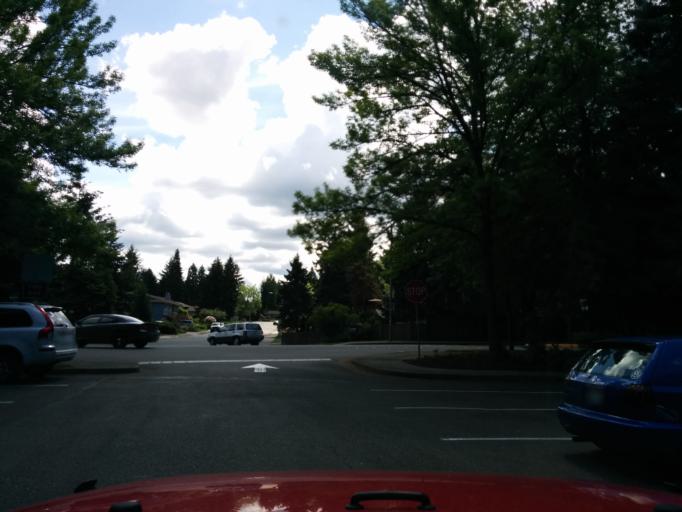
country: US
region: Washington
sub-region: King County
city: Redmond
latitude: 47.6668
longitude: -122.1475
